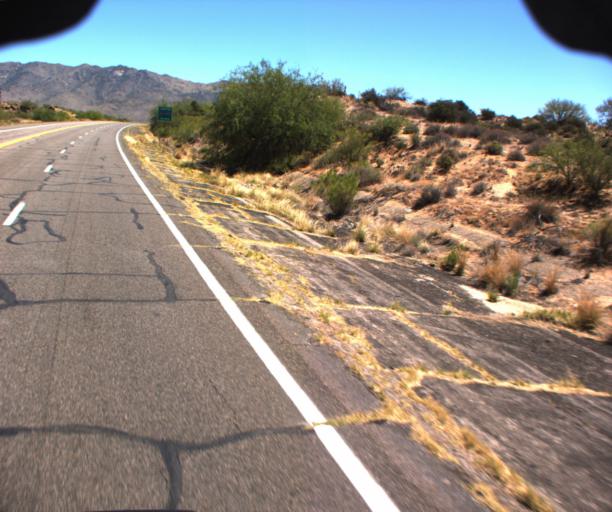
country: US
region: Arizona
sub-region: Yavapai County
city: Congress
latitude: 34.1761
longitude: -112.8316
